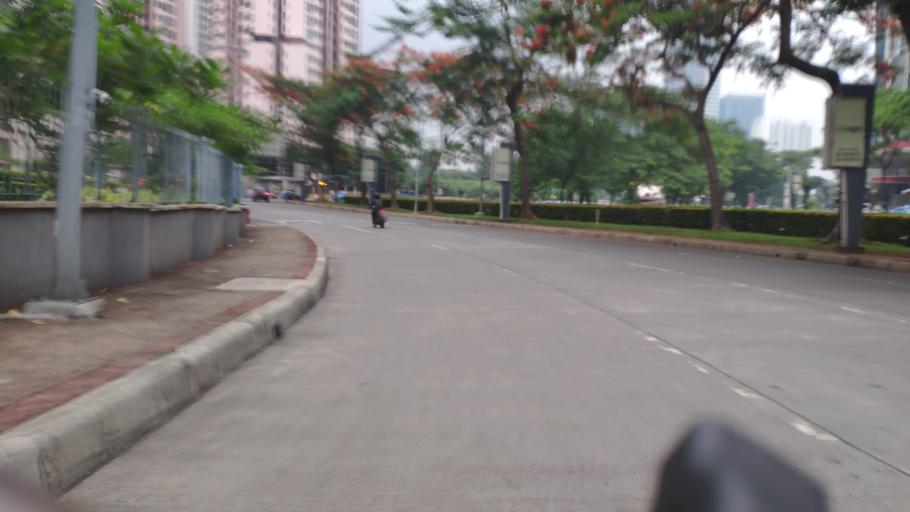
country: ID
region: Jakarta Raya
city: Jakarta
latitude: -6.2172
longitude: 106.8360
